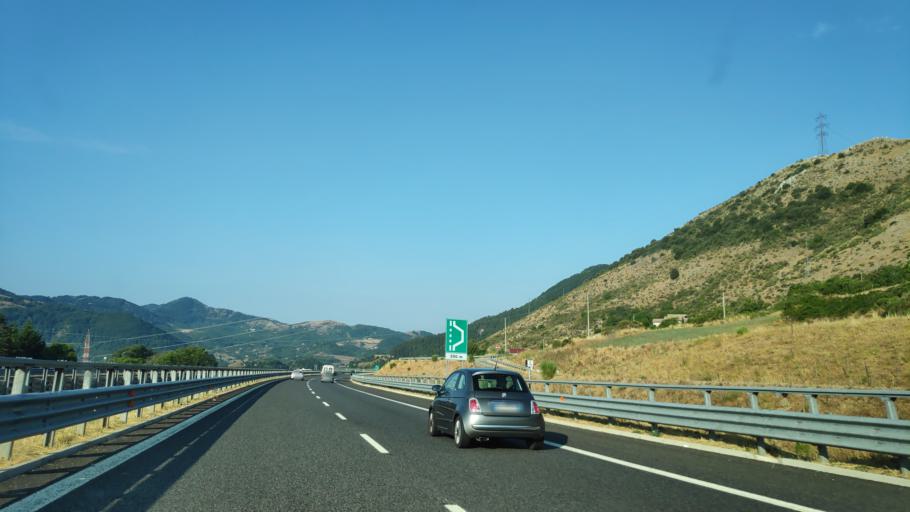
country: IT
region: Calabria
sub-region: Provincia di Cosenza
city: Mormanno
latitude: 39.8872
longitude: 16.0265
